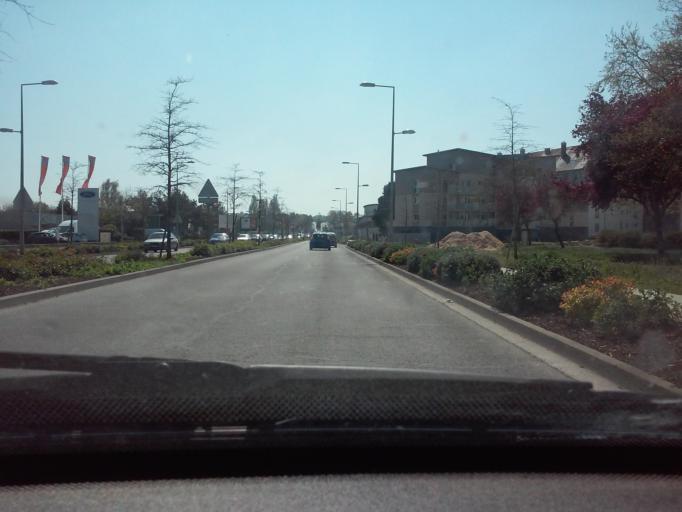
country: FR
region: Brittany
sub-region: Departement d'Ille-et-Vilaine
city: Saint-Malo
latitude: 48.6405
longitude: -1.9902
